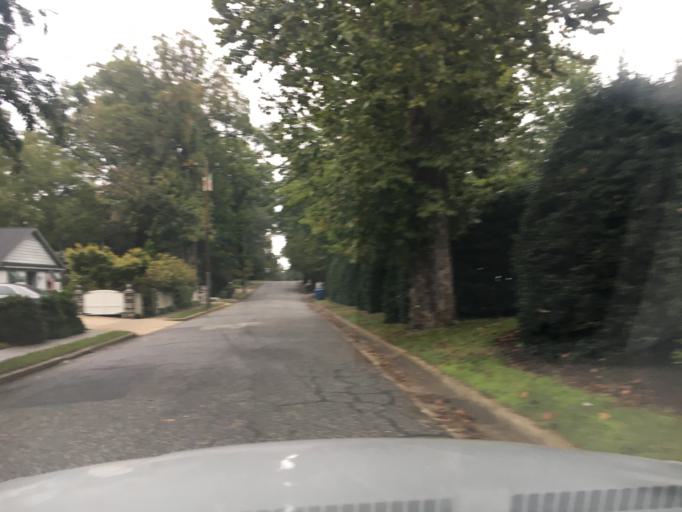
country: US
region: North Carolina
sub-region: Catawba County
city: Hickory
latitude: 35.7345
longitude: -81.3460
